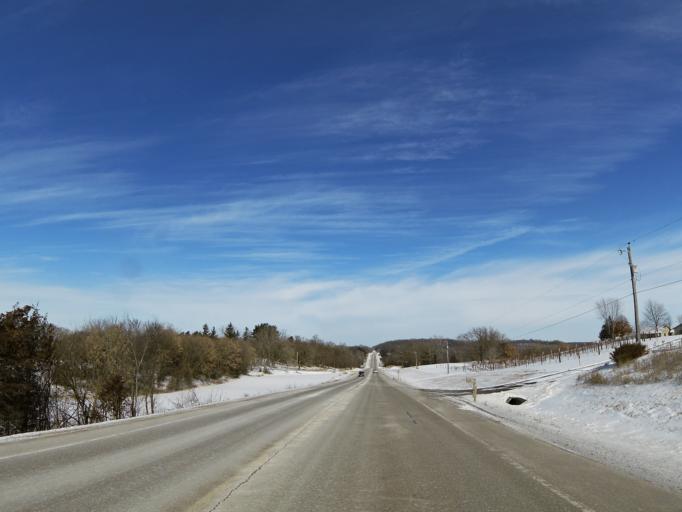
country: US
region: Minnesota
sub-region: Washington County
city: Afton
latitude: 44.8634
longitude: -92.7311
